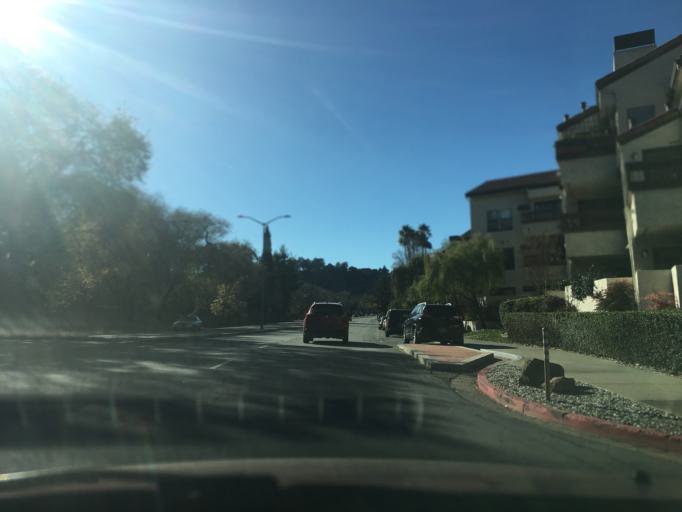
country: US
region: California
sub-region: Contra Costa County
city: Saranap
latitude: 37.8894
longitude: -122.0693
